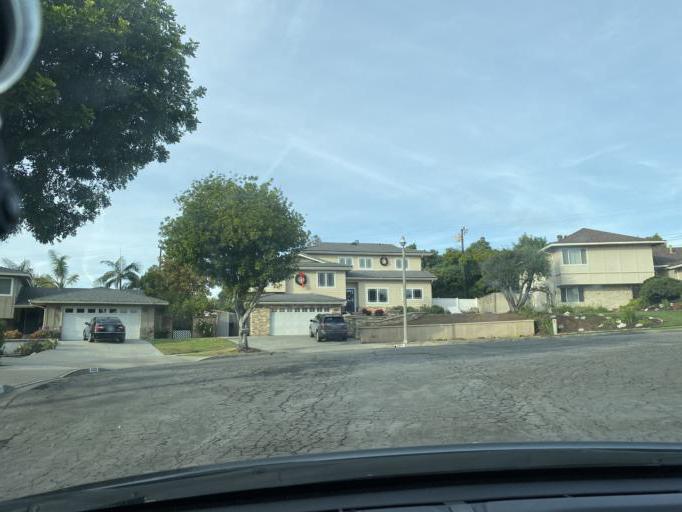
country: US
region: California
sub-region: Orange County
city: Brea
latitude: 33.8991
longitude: -117.8793
